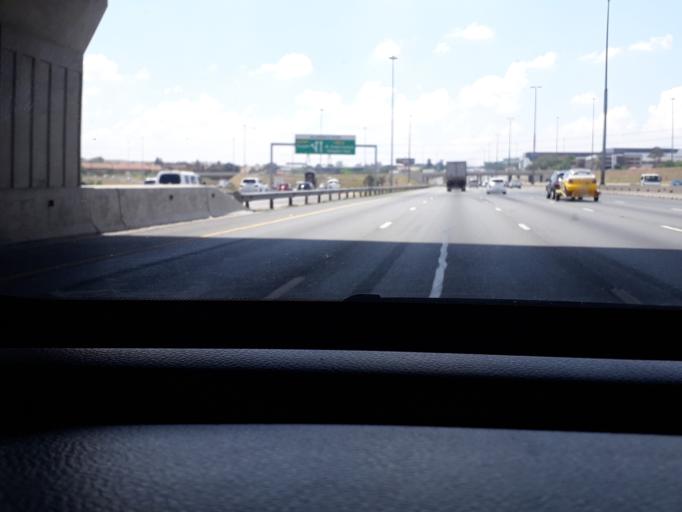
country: ZA
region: Gauteng
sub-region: City of Johannesburg Metropolitan Municipality
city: Midrand
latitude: -26.0200
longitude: 28.1134
